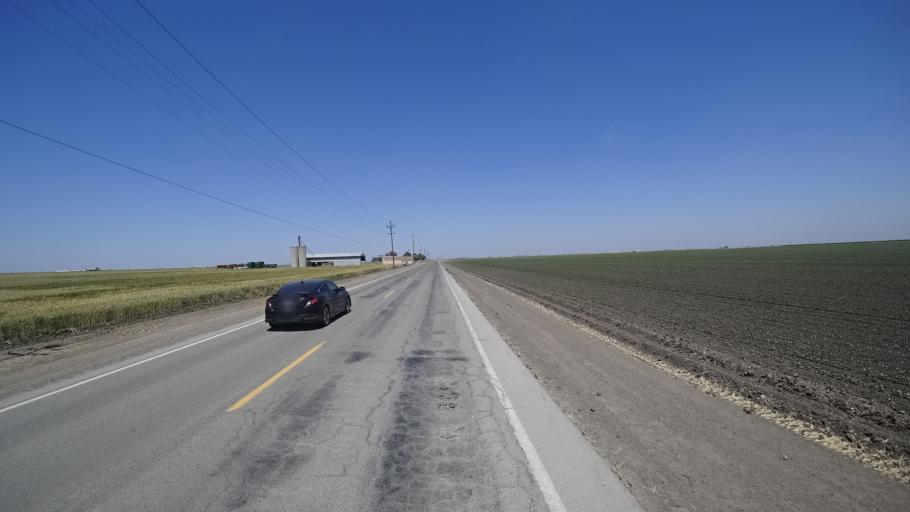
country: US
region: California
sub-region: Kings County
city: Corcoran
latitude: 36.1310
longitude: -119.6444
